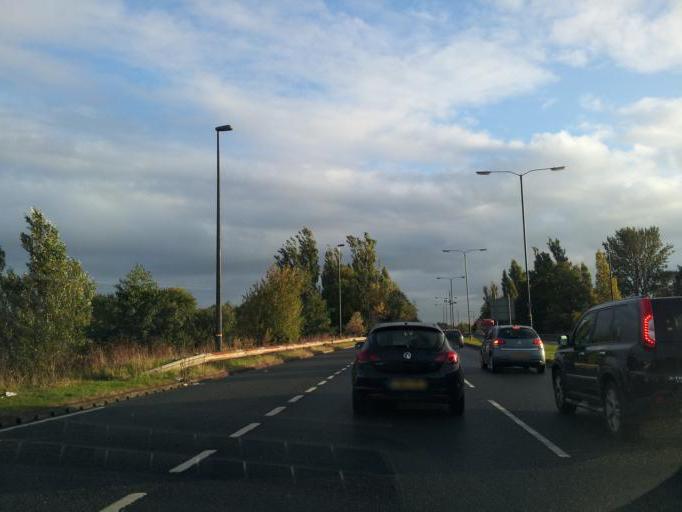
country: GB
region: England
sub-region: City and Borough of Salford
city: Eccles
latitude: 53.4648
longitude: -2.3322
